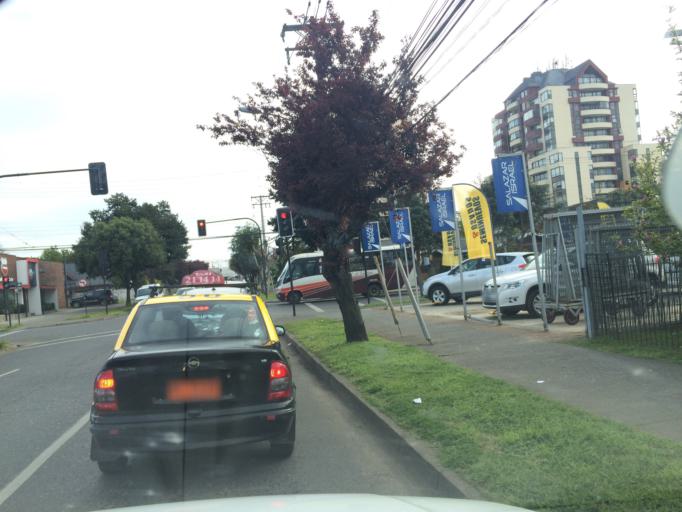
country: CL
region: Araucania
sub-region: Provincia de Cautin
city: Temuco
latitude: -38.7387
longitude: -72.6178
